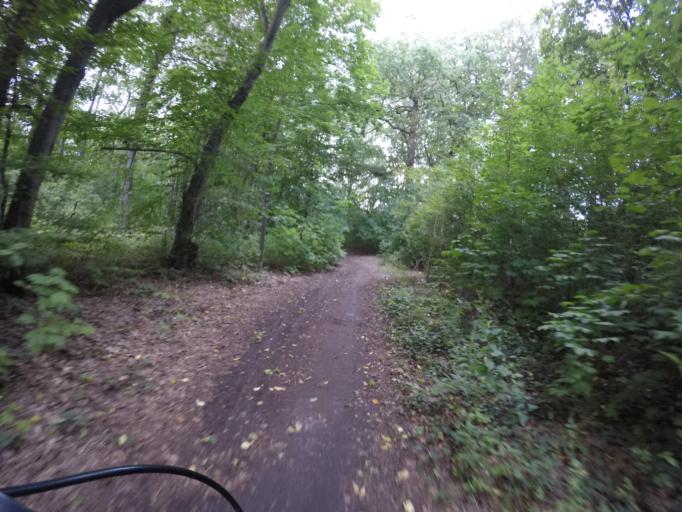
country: DE
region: Brandenburg
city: Werder
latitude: 52.3537
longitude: 12.9805
